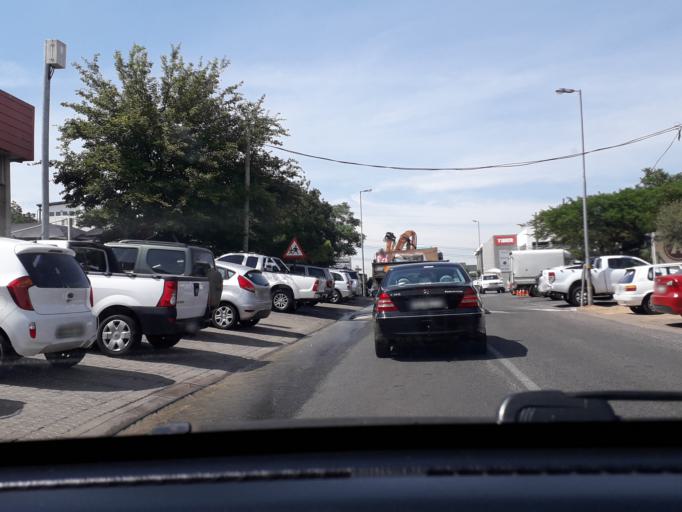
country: ZA
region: Gauteng
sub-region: City of Johannesburg Metropolitan Municipality
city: Modderfontein
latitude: -26.0884
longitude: 28.0811
